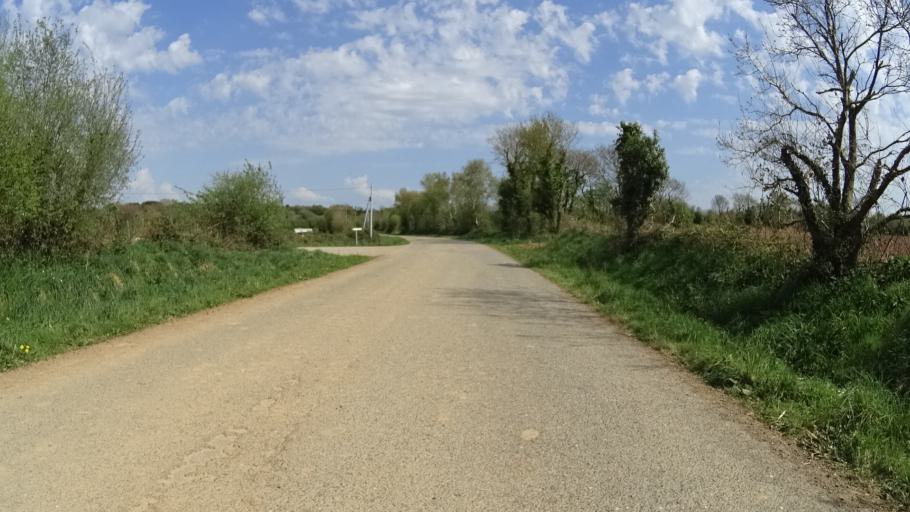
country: FR
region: Brittany
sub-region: Departement du Finistere
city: Sizun
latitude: 48.4267
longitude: -4.0883
